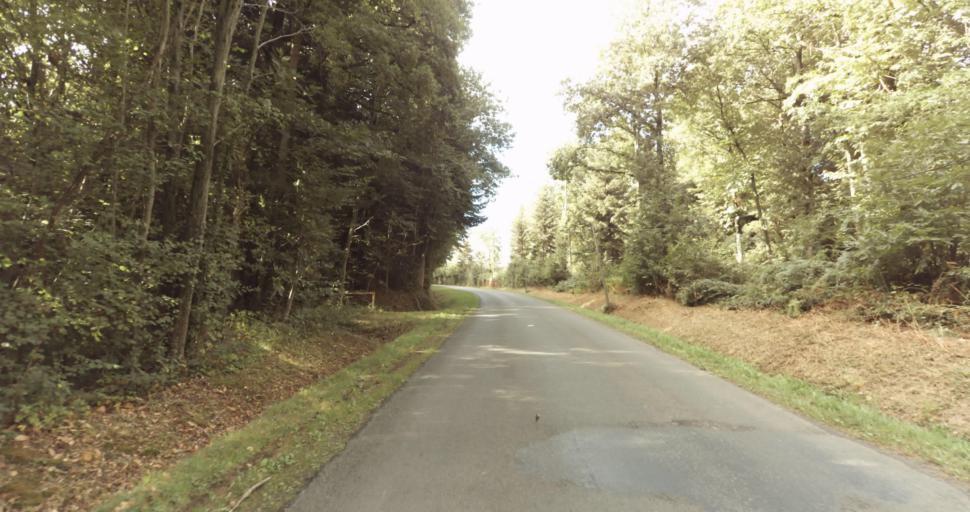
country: FR
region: Lower Normandy
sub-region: Departement de l'Orne
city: Gace
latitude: 48.8332
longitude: 0.2400
